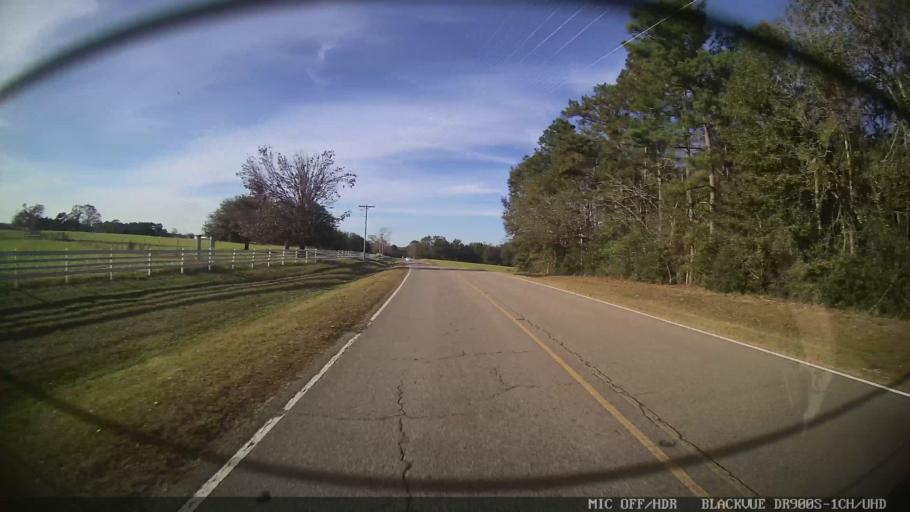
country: US
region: Mississippi
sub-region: Lamar County
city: Purvis
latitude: 31.1940
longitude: -89.2884
